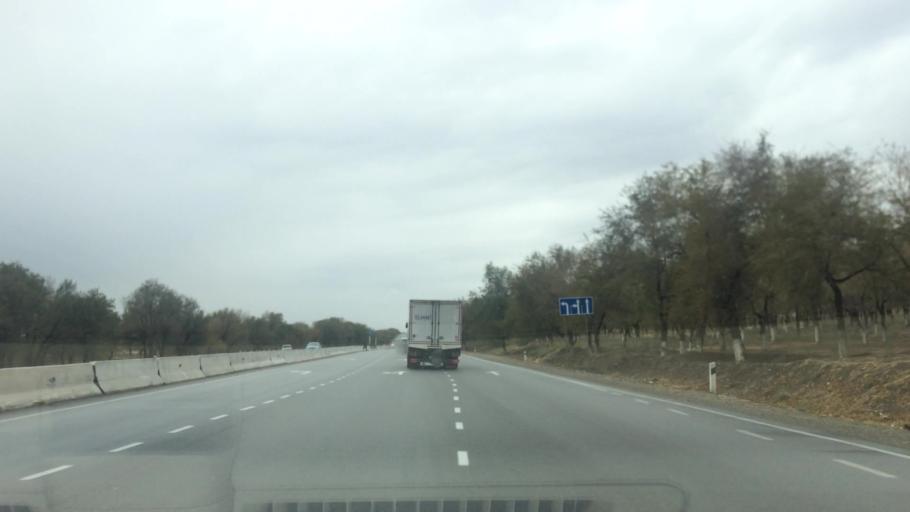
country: UZ
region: Samarqand
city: Bulung'ur
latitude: 39.9010
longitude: 67.5014
